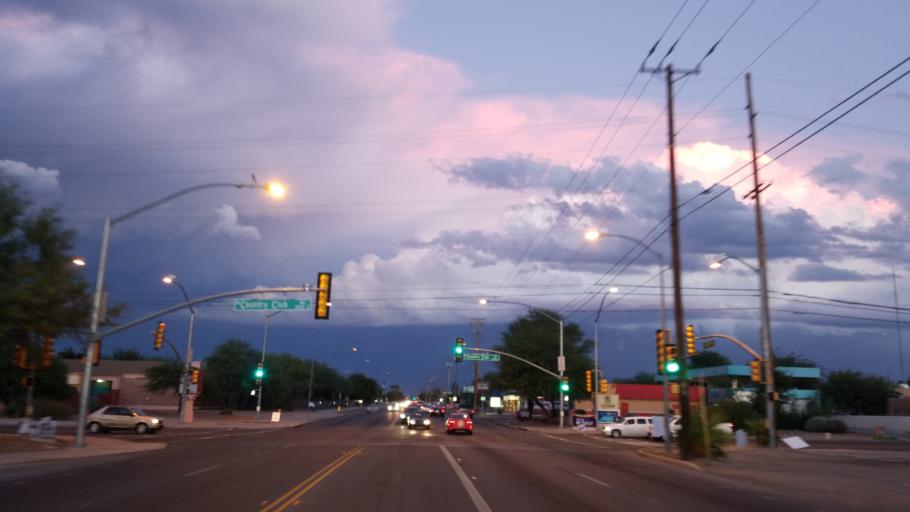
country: US
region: Arizona
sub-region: Pima County
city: Tucson
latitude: 32.2504
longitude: -110.9274
